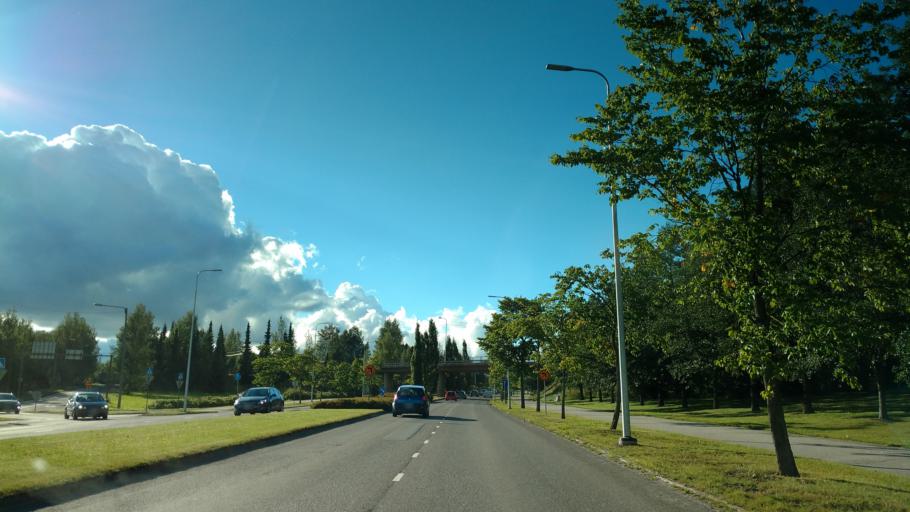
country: FI
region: Varsinais-Suomi
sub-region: Salo
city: Salo
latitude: 60.3922
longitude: 23.1120
